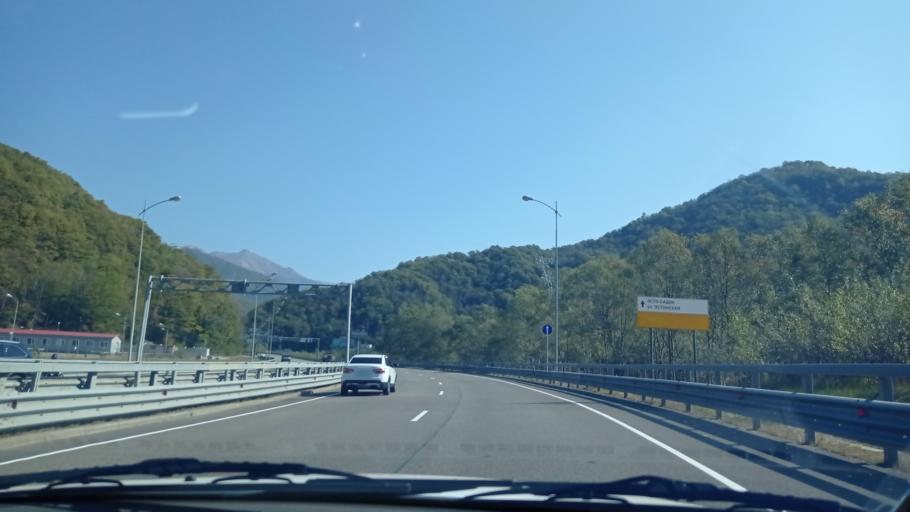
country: RU
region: Krasnodarskiy
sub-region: Sochi City
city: Krasnaya Polyana
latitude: 43.6853
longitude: 40.2373
